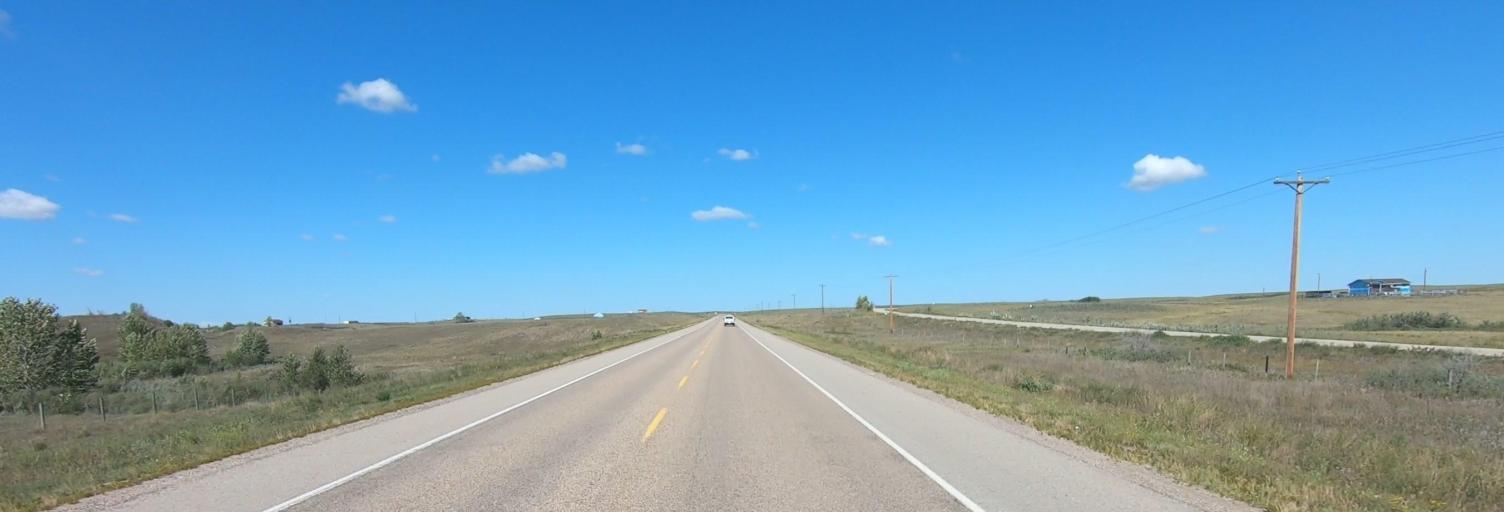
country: CA
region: Alberta
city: Strathmore
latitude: 50.8601
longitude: -113.1391
